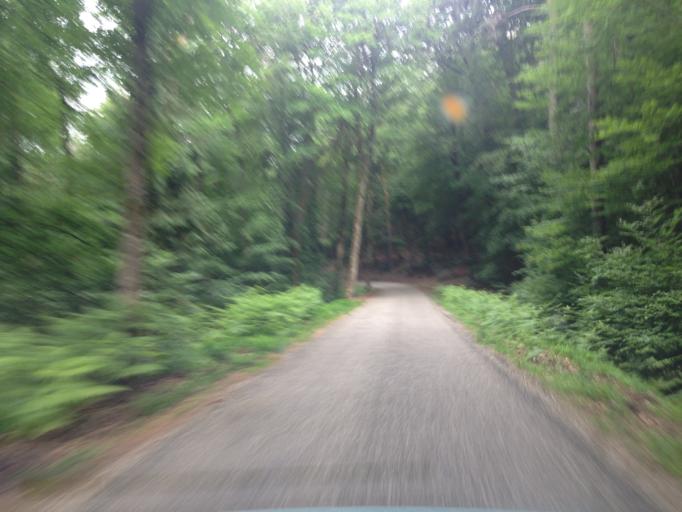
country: FR
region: Alsace
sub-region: Departement du Bas-Rhin
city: Neuwiller-les-Saverne
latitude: 48.8485
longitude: 7.3771
